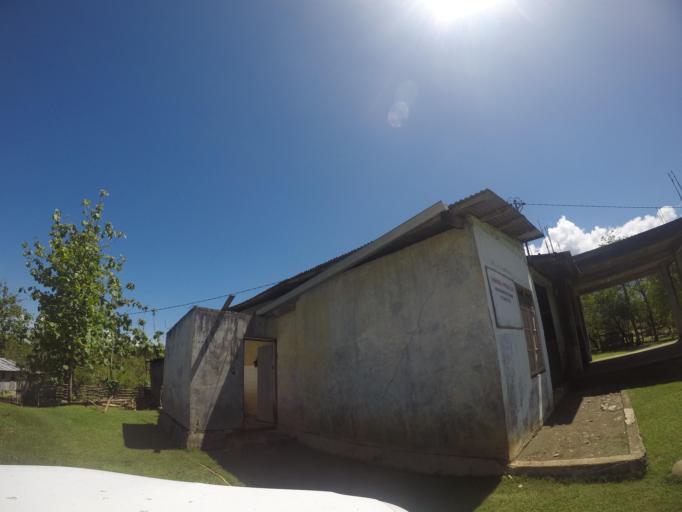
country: TL
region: Bobonaro
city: Maliana
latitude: -8.9670
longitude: 125.2088
